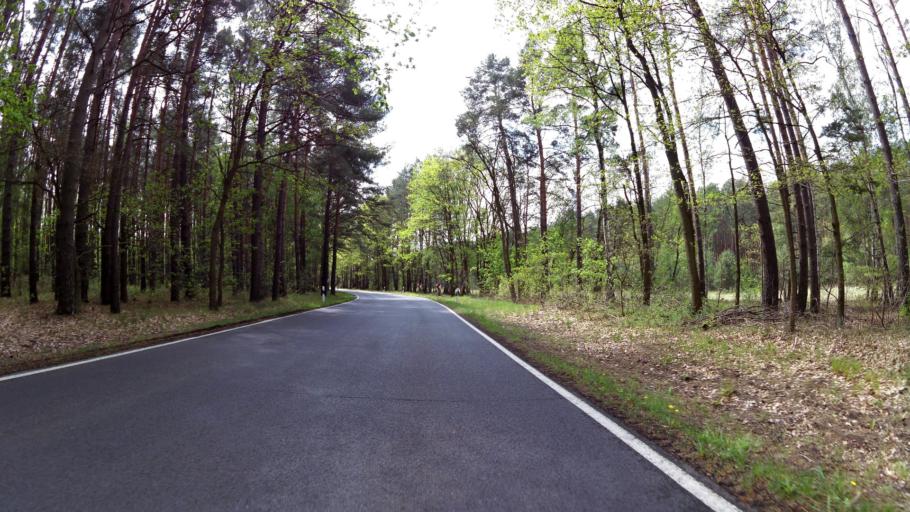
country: DE
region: Brandenburg
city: Bestensee
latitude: 52.2791
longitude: 13.7340
